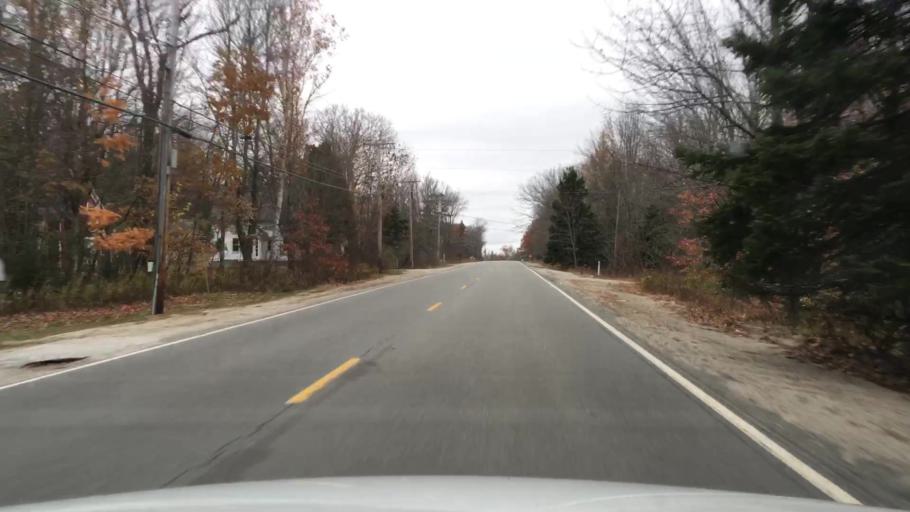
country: US
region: Maine
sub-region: Hancock County
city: Sedgwick
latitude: 44.3988
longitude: -68.5888
